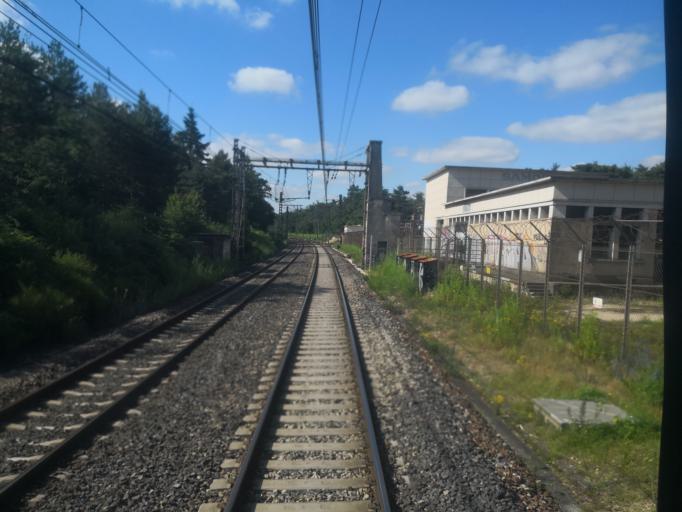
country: FR
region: Ile-de-France
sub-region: Departement de Seine-et-Marne
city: Samoreau
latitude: 48.4353
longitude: 2.7382
